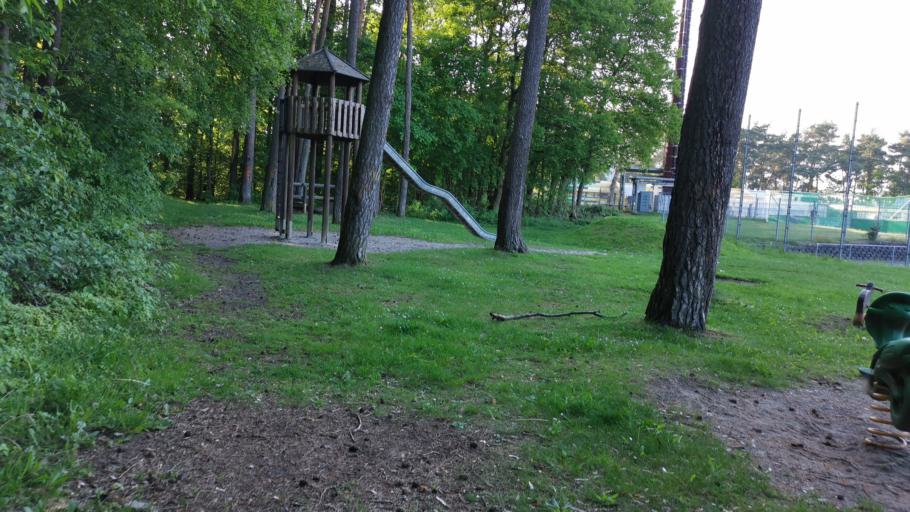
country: DE
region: Saarland
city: Sankt Ingbert
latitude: 49.2617
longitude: 7.1657
